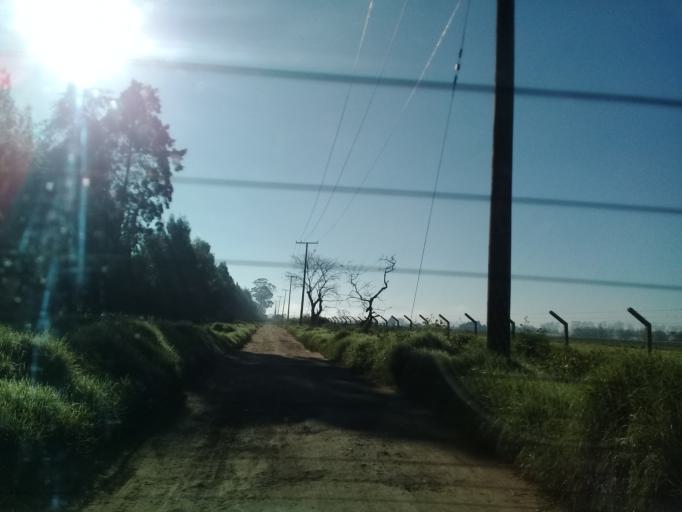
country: CO
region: Cundinamarca
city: Funza
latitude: 4.7591
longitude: -74.2271
